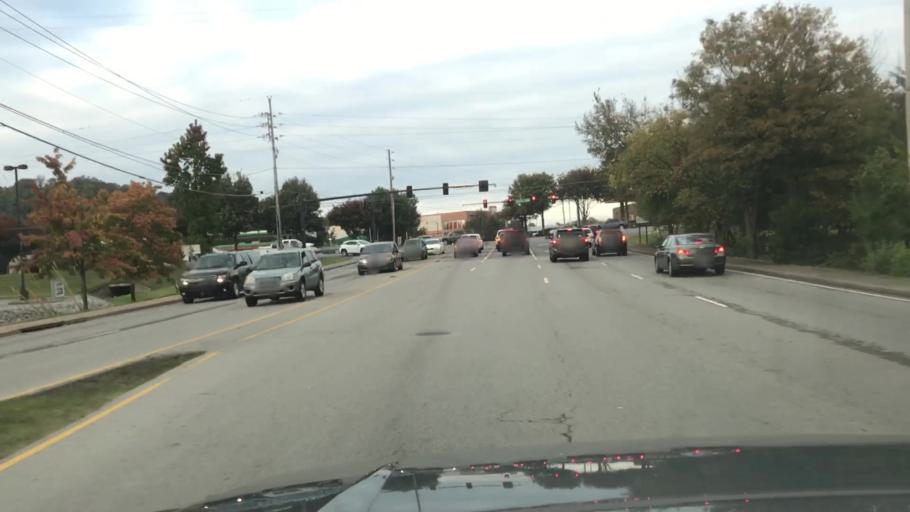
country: US
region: Tennessee
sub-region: Williamson County
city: Brentwood Estates
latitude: 35.9662
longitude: -86.8138
